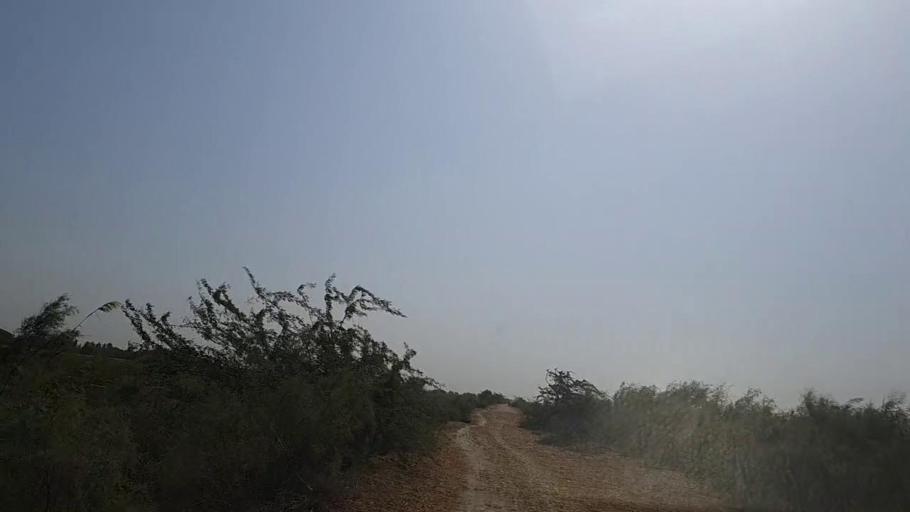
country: PK
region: Sindh
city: Daro Mehar
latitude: 24.7131
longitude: 68.1209
